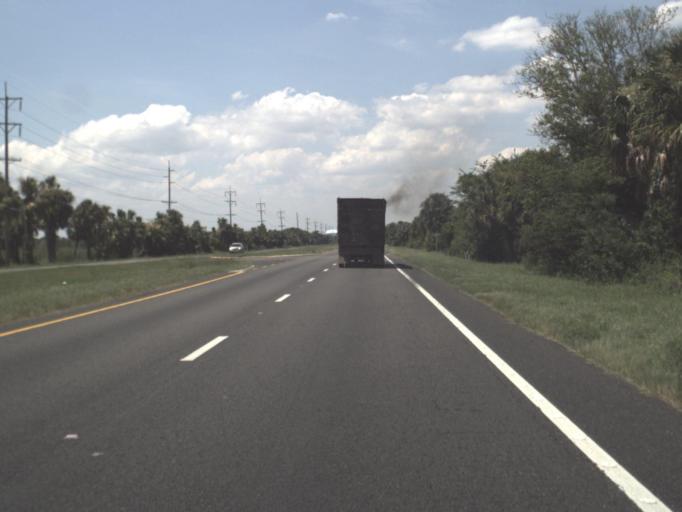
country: US
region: Florida
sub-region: Hillsborough County
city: Gibsonton
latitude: 27.8801
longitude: -82.3939
